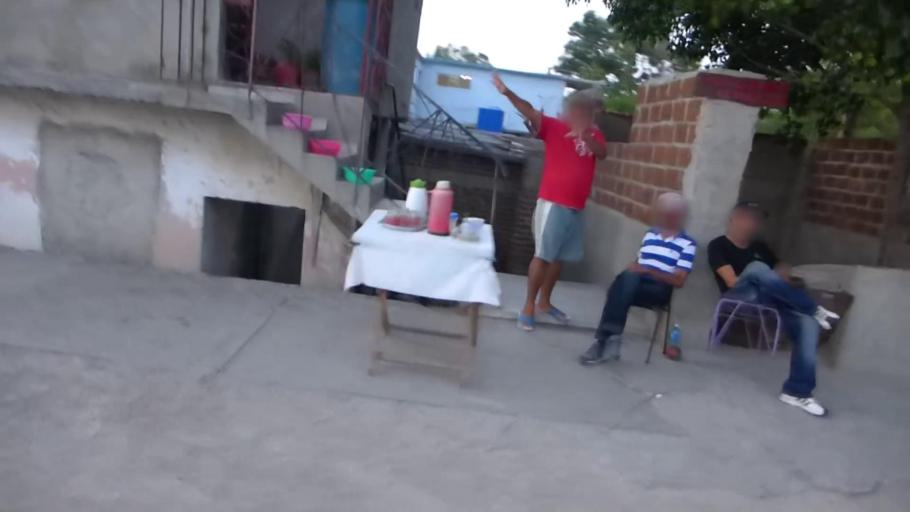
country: CU
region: Camaguey
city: Camaguey
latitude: 21.3735
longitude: -77.9176
